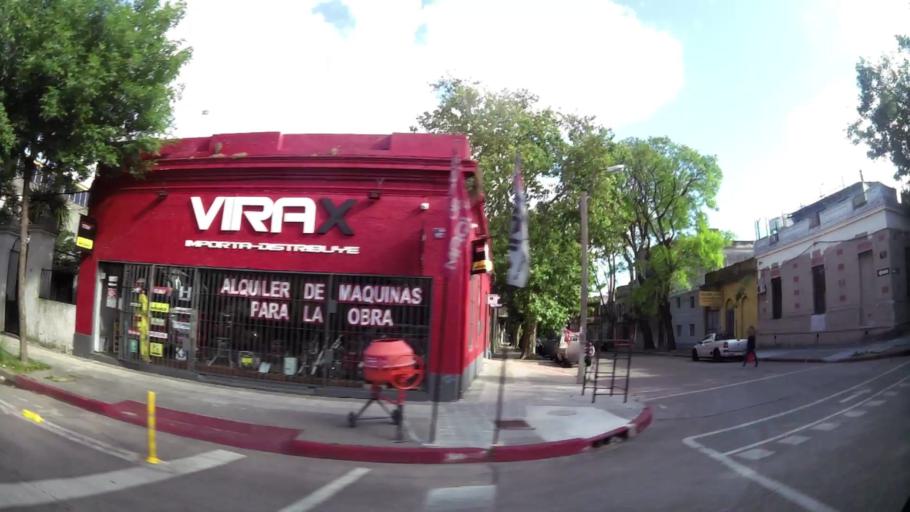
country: UY
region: Montevideo
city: Montevideo
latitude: -34.8903
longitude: -56.1802
